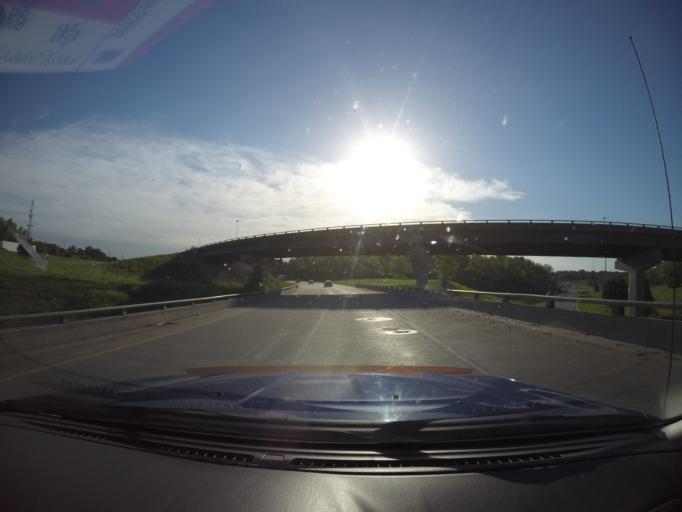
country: US
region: Kansas
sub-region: Wyandotte County
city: Kansas City
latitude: 39.1466
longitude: -94.6575
